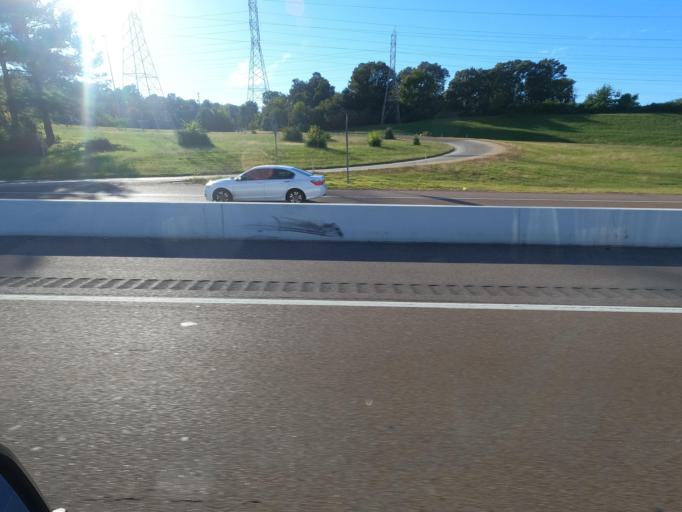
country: US
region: Tennessee
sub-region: Shelby County
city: Germantown
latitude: 35.1316
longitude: -89.8669
